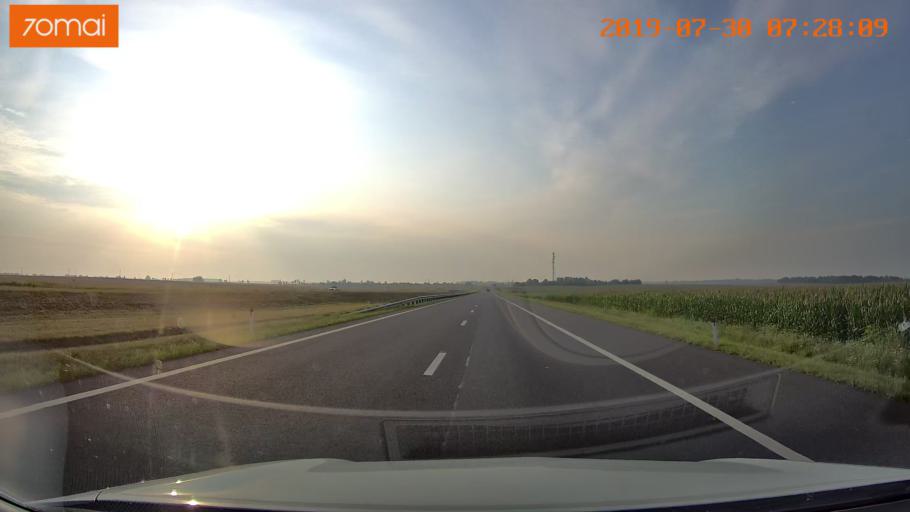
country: RU
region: Kaliningrad
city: Gvardeysk
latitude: 54.6787
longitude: 20.9059
